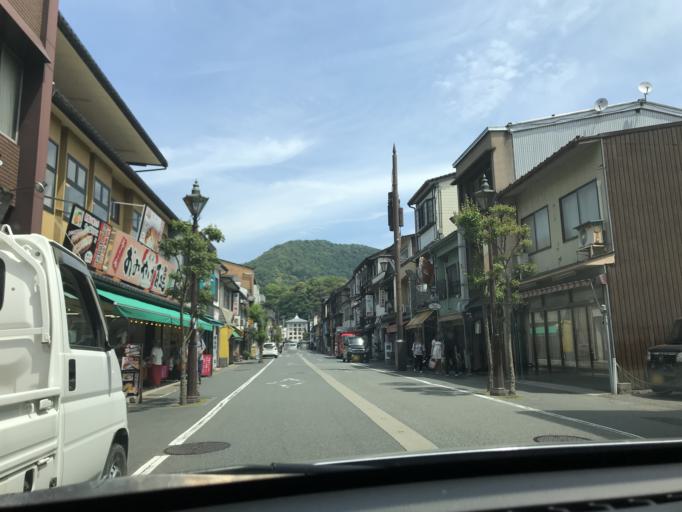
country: JP
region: Hyogo
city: Toyooka
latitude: 35.6246
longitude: 134.8129
